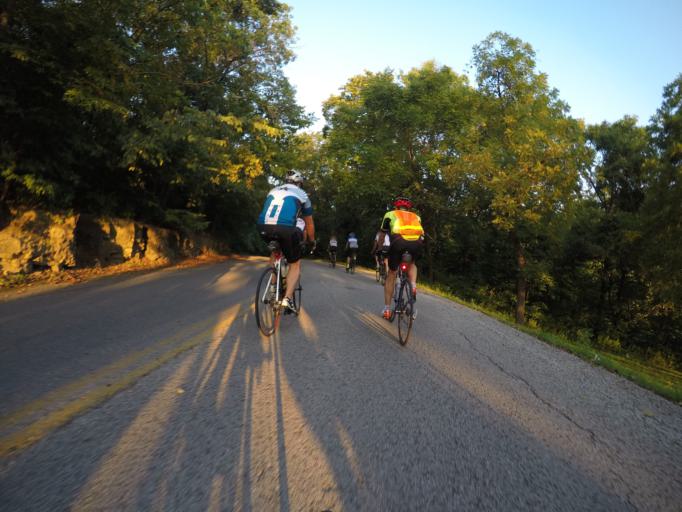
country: US
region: Kansas
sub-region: Wyandotte County
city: Edwardsville
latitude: 39.1519
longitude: -94.7903
